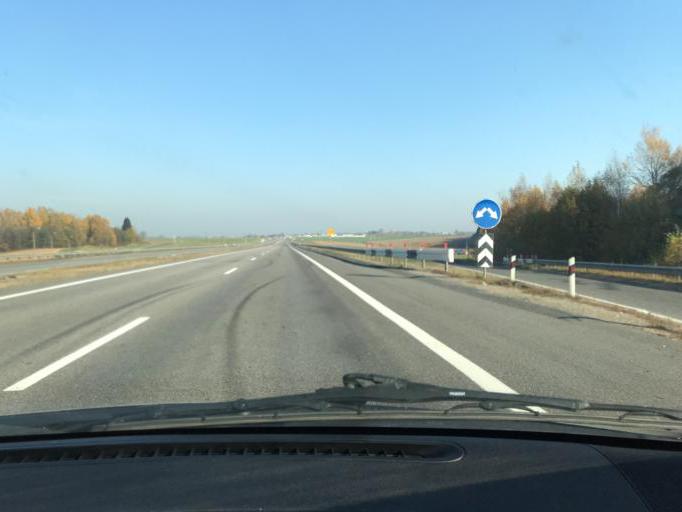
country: BY
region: Vitebsk
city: Horad Orsha
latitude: 54.5904
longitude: 30.3434
